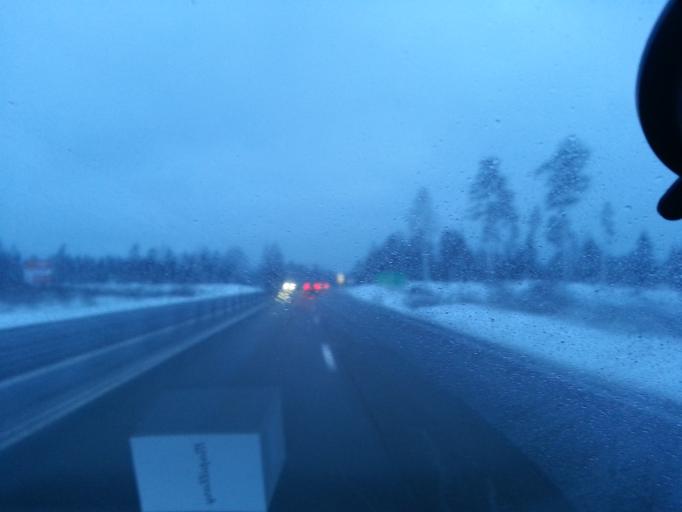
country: SE
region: Kronoberg
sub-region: Ljungby Kommun
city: Lagan
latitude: 56.9209
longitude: 13.9742
